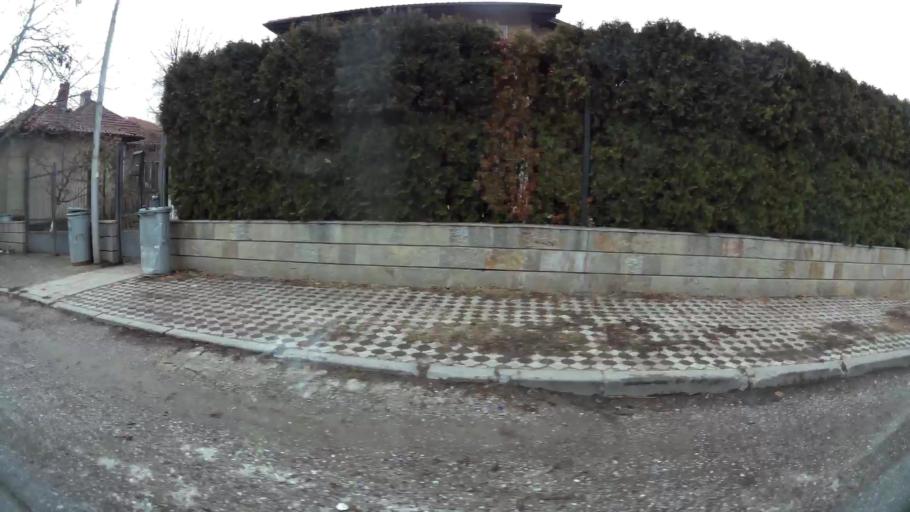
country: BG
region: Sofiya
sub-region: Obshtina Bozhurishte
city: Bozhurishte
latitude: 42.7446
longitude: 23.2618
